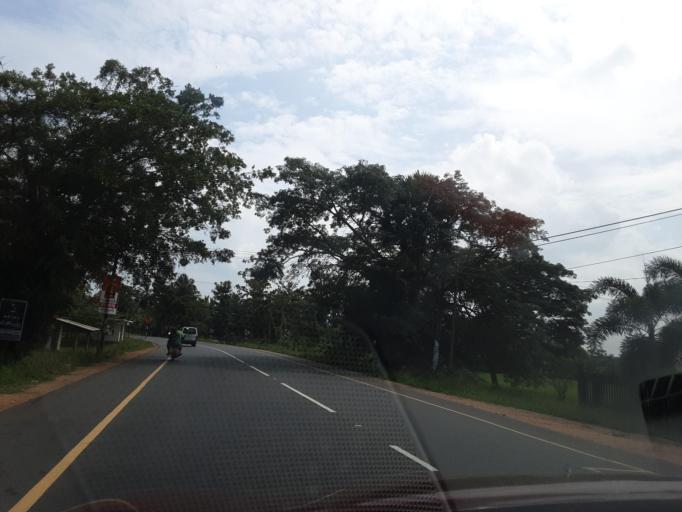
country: LK
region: North Central
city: Anuradhapura
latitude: 8.5055
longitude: 80.5082
